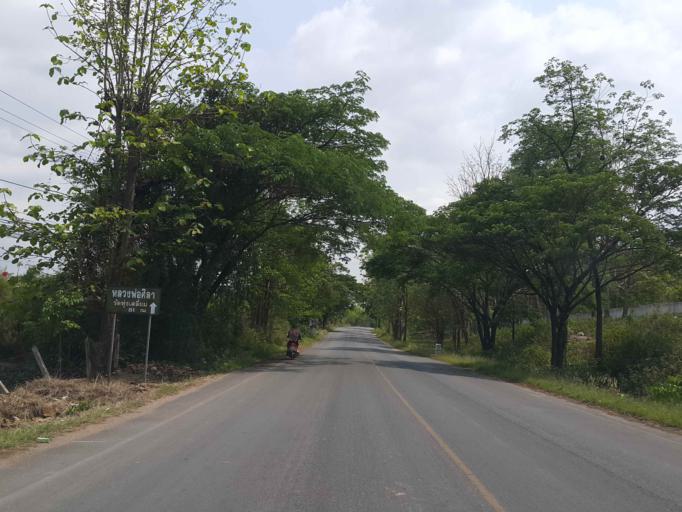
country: TH
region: Lampang
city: Thoen
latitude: 17.5948
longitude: 99.3318
